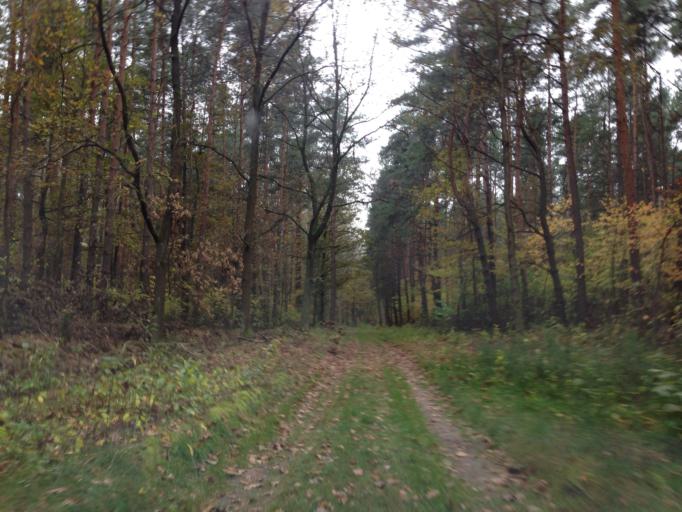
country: PL
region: Masovian Voivodeship
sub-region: Powiat warszawski zachodni
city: Leszno
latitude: 52.2734
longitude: 20.6046
